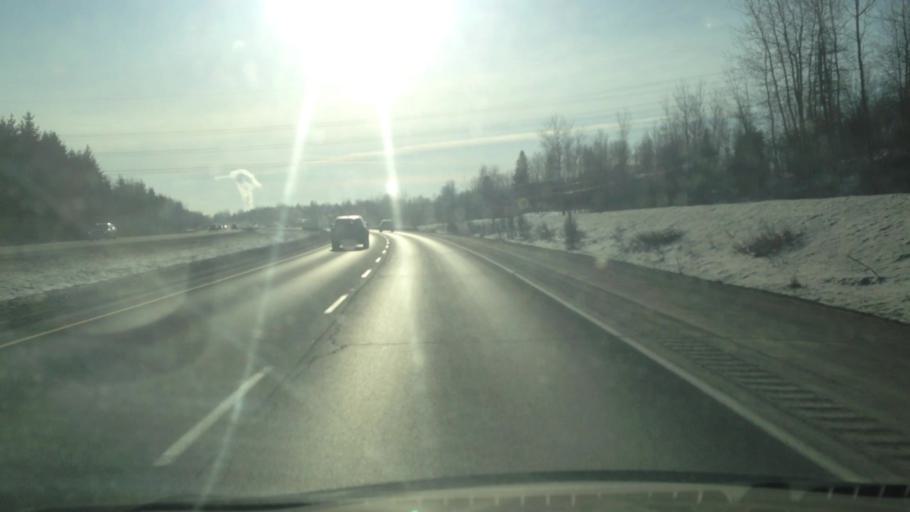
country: CA
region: Quebec
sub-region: Laurentides
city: Prevost
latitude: 45.8232
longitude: -74.0570
